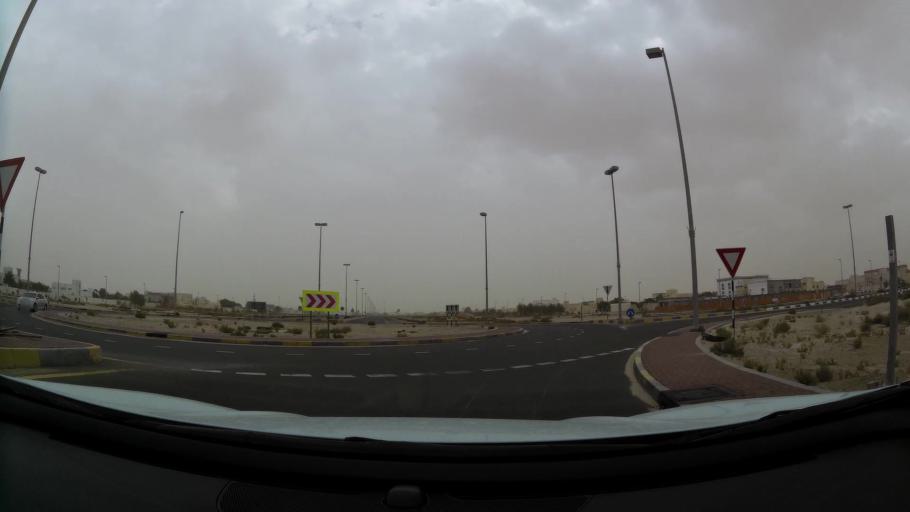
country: AE
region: Abu Dhabi
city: Abu Dhabi
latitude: 24.4030
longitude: 54.7345
